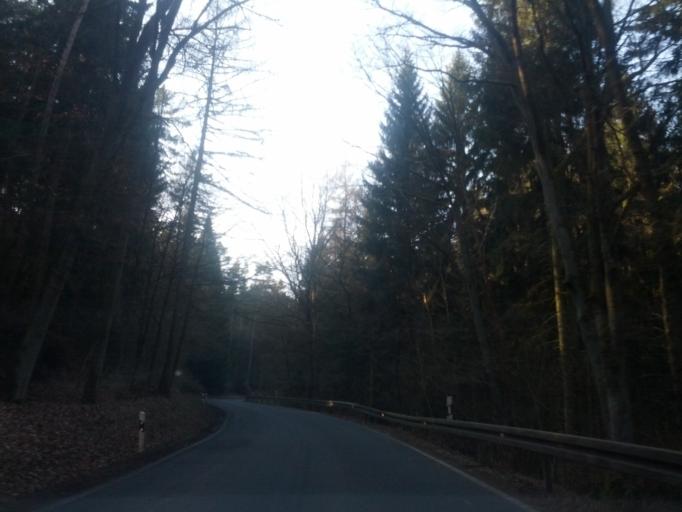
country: DE
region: Thuringia
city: Creuzburg
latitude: 51.0681
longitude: 10.2342
